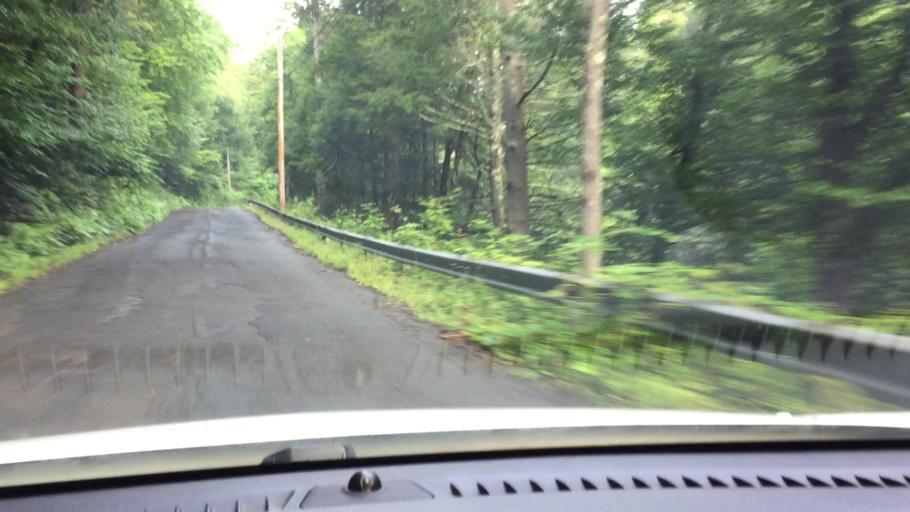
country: US
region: Massachusetts
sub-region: Hampshire County
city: Chesterfield
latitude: 42.3099
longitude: -72.9147
